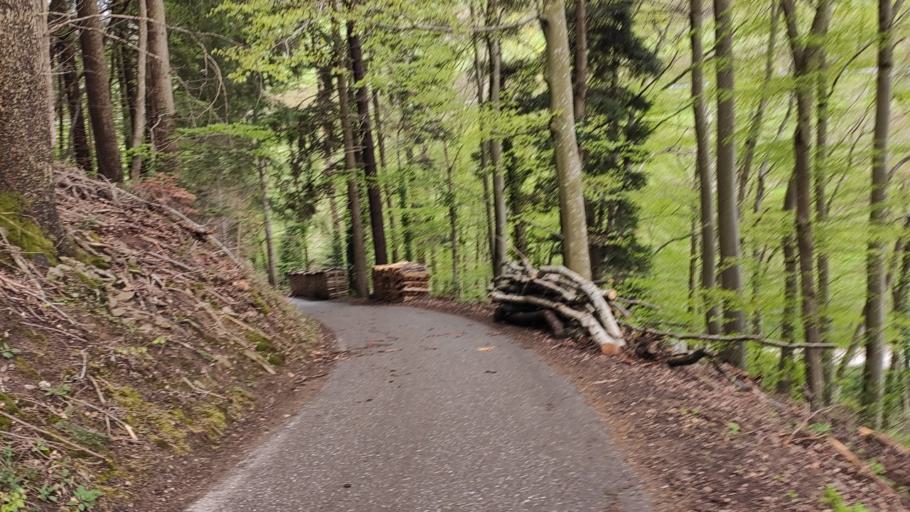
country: DE
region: Baden-Wuerttemberg
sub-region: Freiburg Region
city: Solden
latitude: 47.9105
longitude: 7.8400
